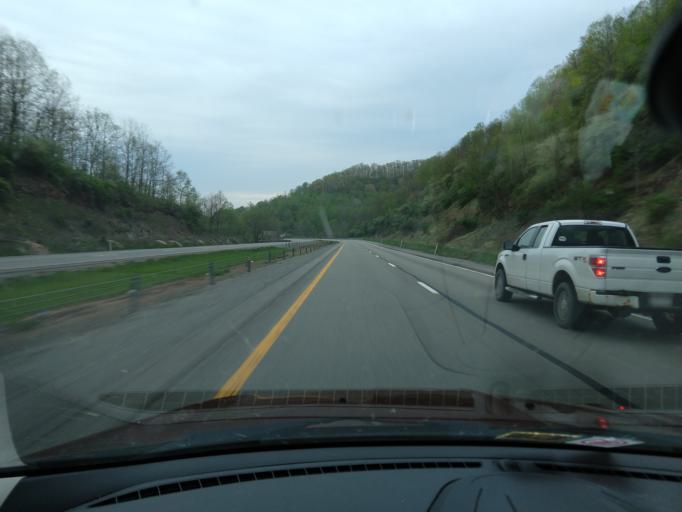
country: US
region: West Virginia
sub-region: Lewis County
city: Weston
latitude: 39.0137
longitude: -80.4846
